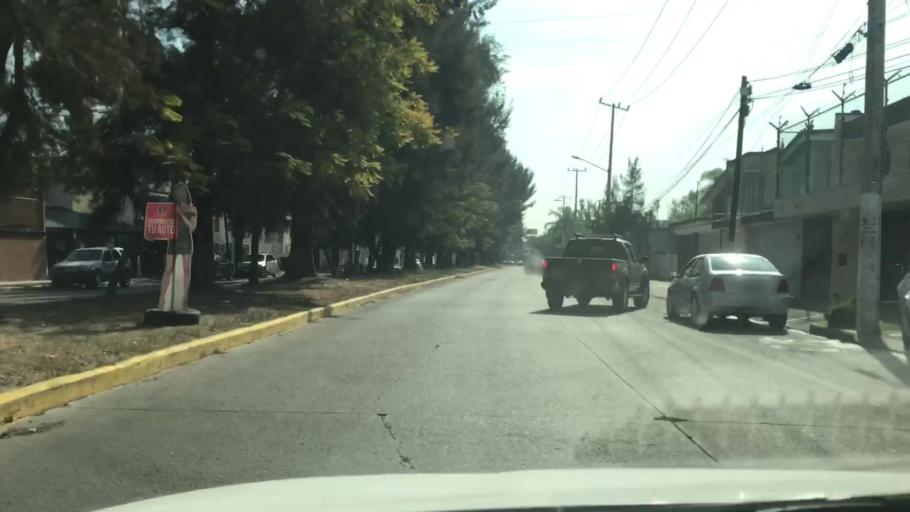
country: MX
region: Jalisco
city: Guadalajara
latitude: 20.6450
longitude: -103.4027
